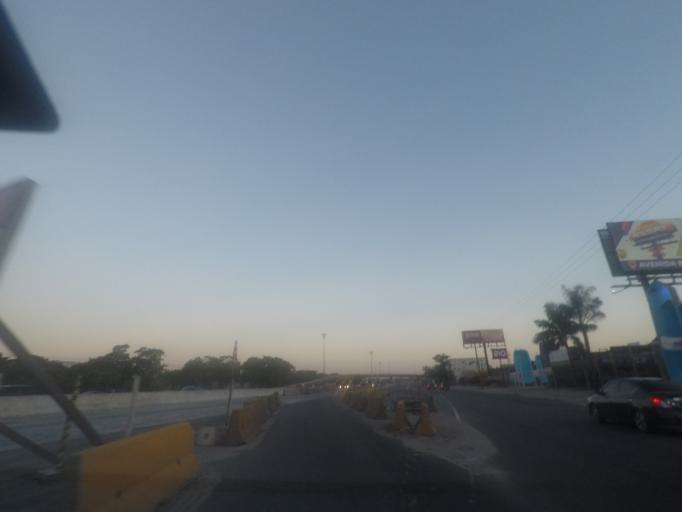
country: BR
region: Rio de Janeiro
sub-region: Duque De Caxias
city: Duque de Caxias
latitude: -22.8237
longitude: -43.2790
